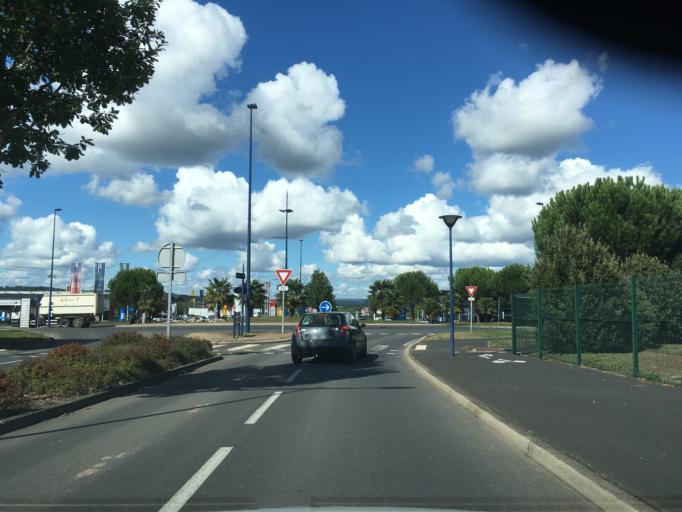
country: FR
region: Limousin
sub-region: Departement de la Correze
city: Saint-Pantaleon-de-Larche
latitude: 45.1392
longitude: 1.4777
